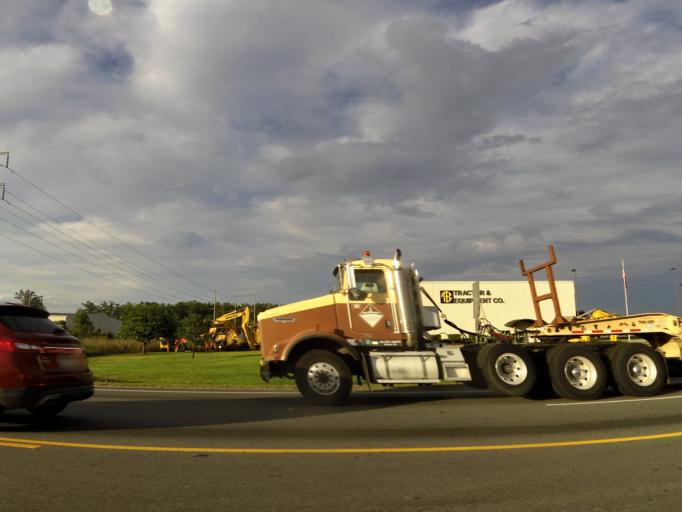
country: US
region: Georgia
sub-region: Chatham County
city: Pooler
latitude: 32.1053
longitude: -81.2273
